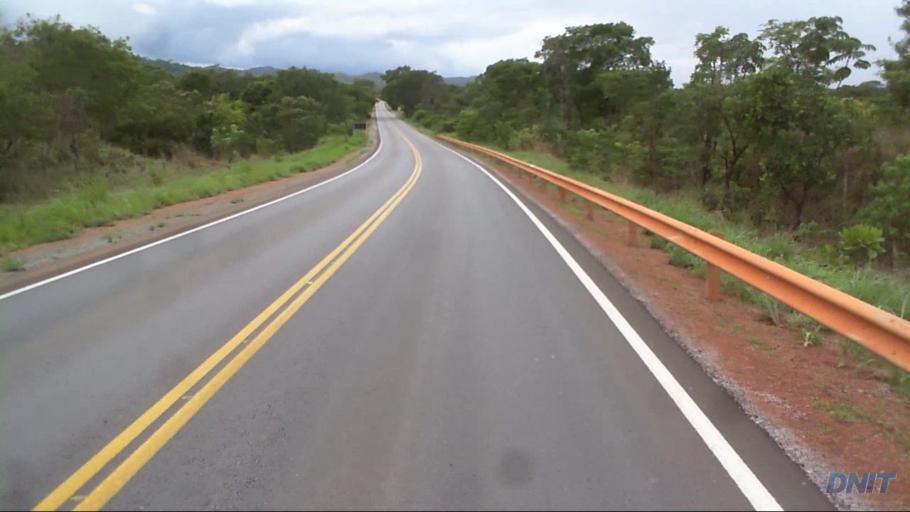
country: BR
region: Goias
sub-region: Padre Bernardo
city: Padre Bernardo
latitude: -15.4185
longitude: -48.1993
